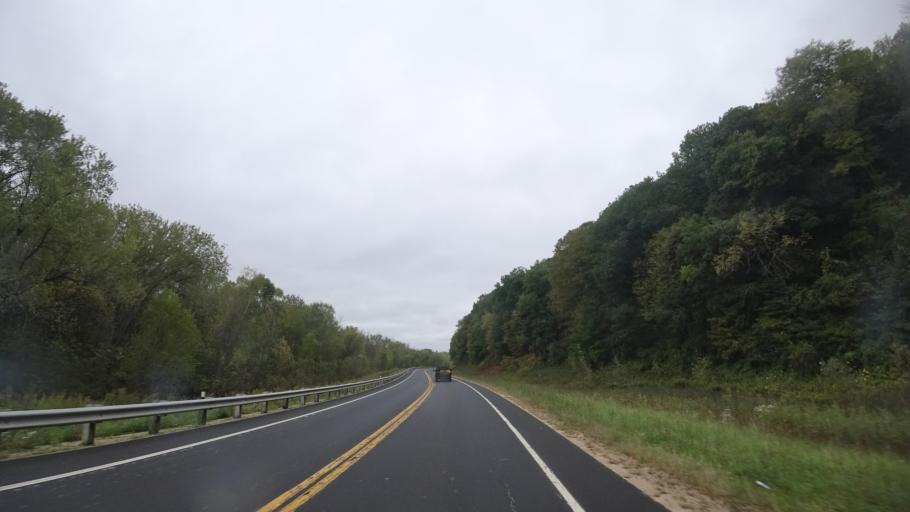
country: US
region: Wisconsin
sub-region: Grant County
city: Boscobel
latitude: 43.1435
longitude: -90.7344
